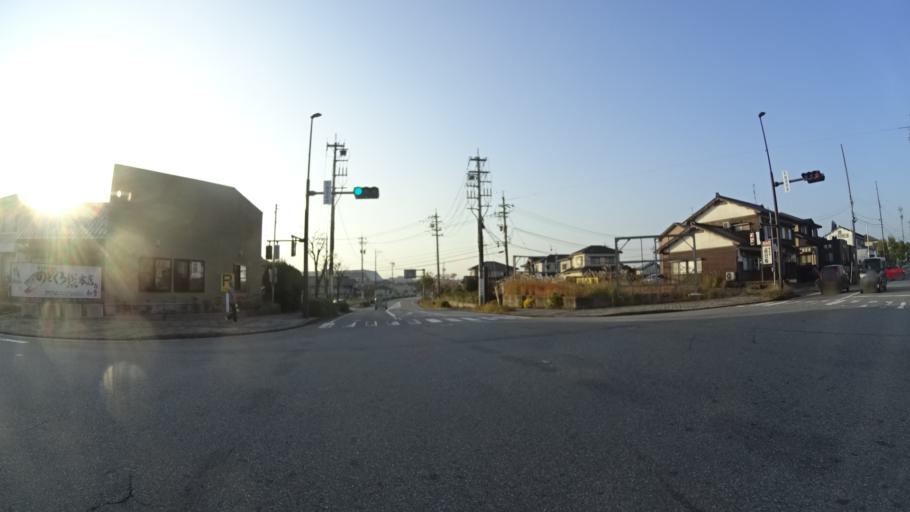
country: JP
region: Ishikawa
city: Nanao
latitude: 37.0836
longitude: 136.9257
